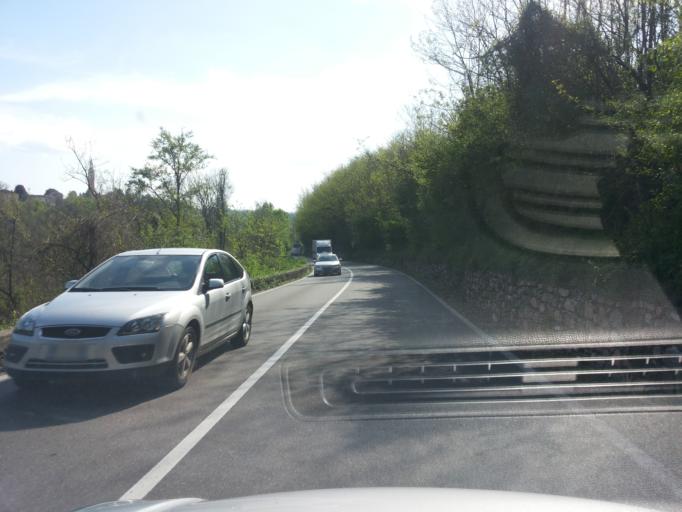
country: IT
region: Lombardy
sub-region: Provincia di Varese
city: Malnate
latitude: 45.8079
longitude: 8.8795
